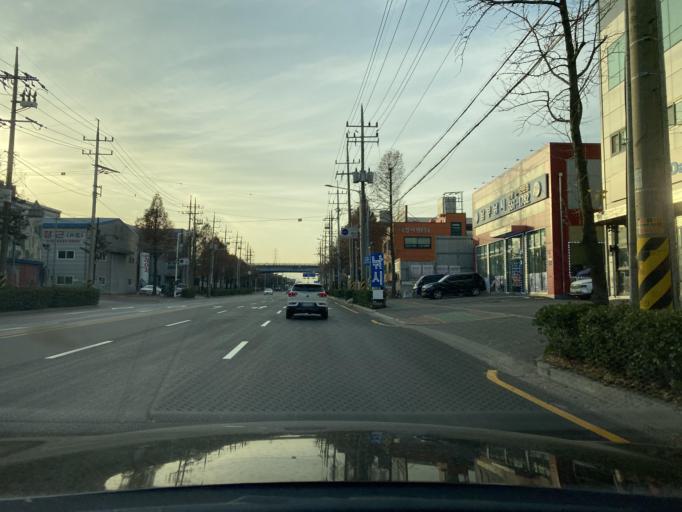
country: KR
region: Incheon
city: Incheon
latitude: 37.4993
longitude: 126.6507
